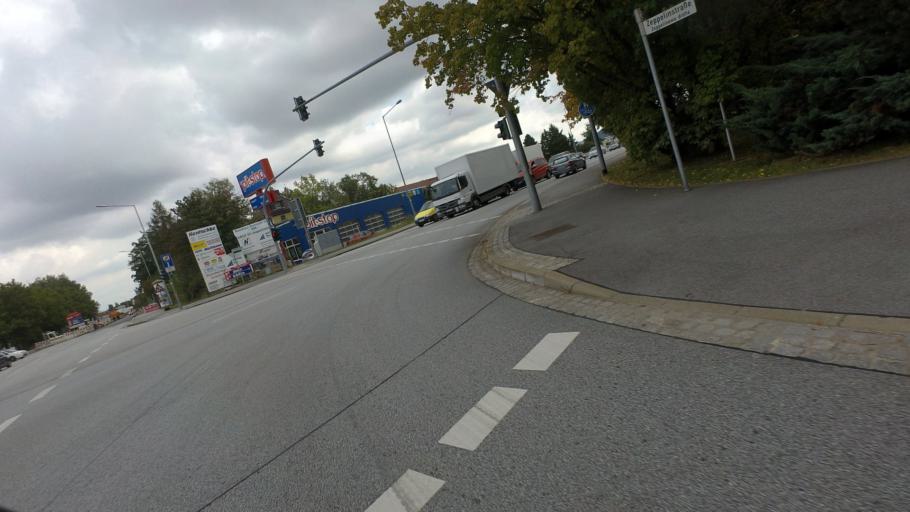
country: DE
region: Saxony
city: Bautzen
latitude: 51.1687
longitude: 14.4255
